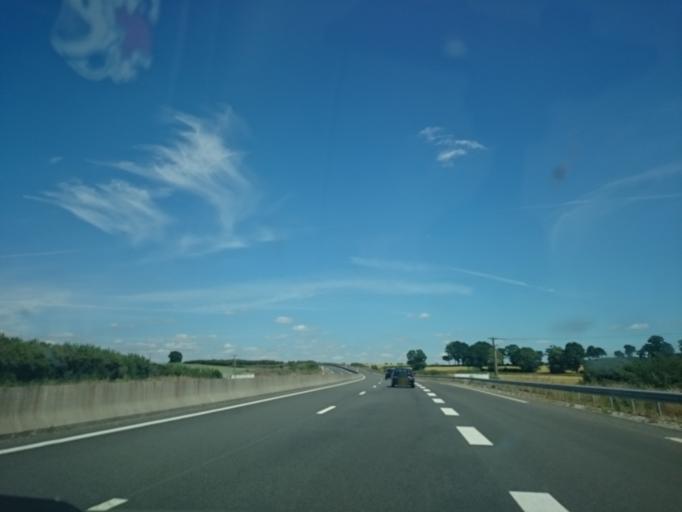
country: FR
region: Brittany
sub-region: Departement des Cotes-d'Armor
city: Gouarec
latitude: 48.2315
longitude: -3.1585
